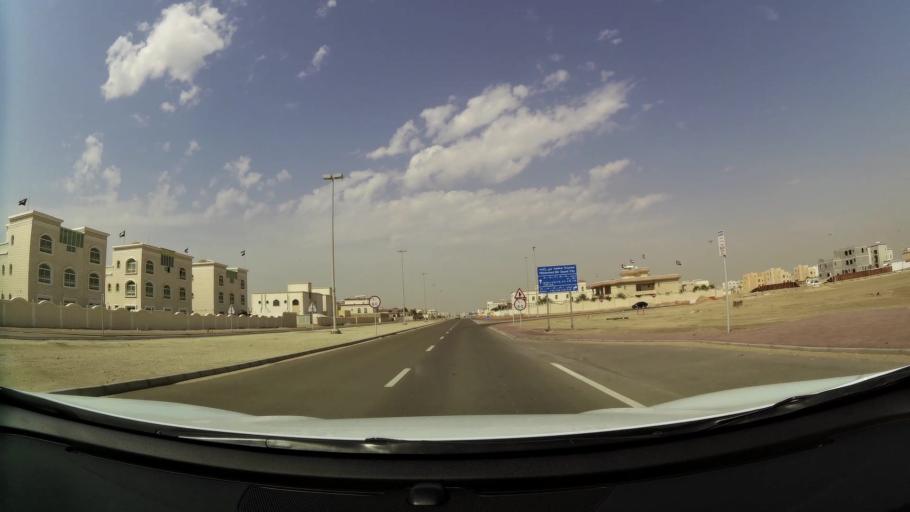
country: AE
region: Abu Dhabi
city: Abu Dhabi
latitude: 24.3176
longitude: 54.5525
